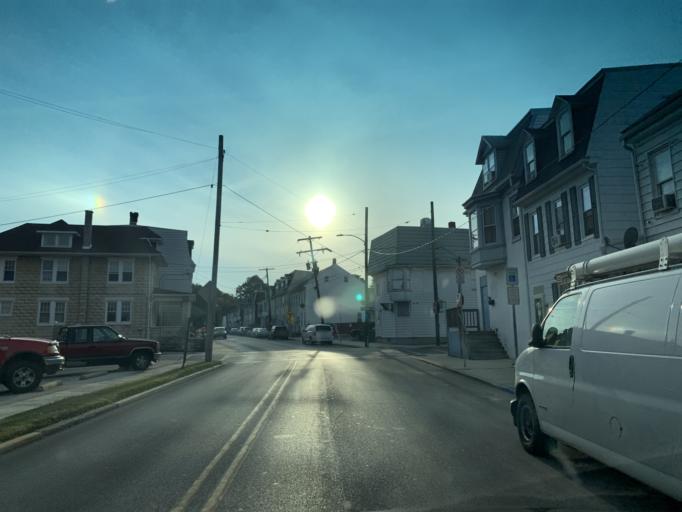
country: US
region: Pennsylvania
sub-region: York County
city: West York
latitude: 39.9537
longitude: -76.7404
